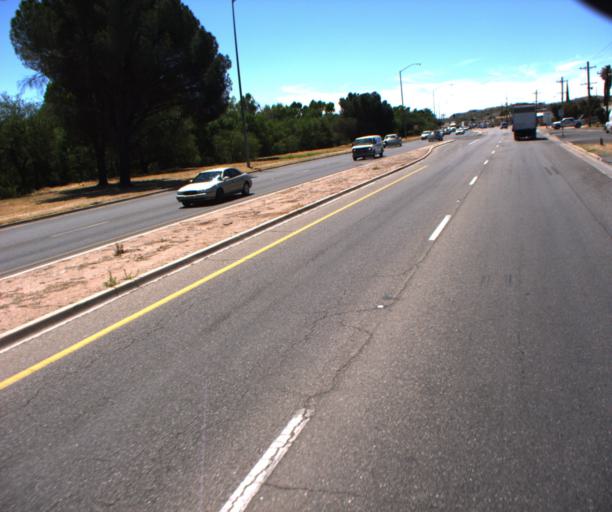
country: US
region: Arizona
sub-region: Santa Cruz County
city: Nogales
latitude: 31.3857
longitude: -110.9494
